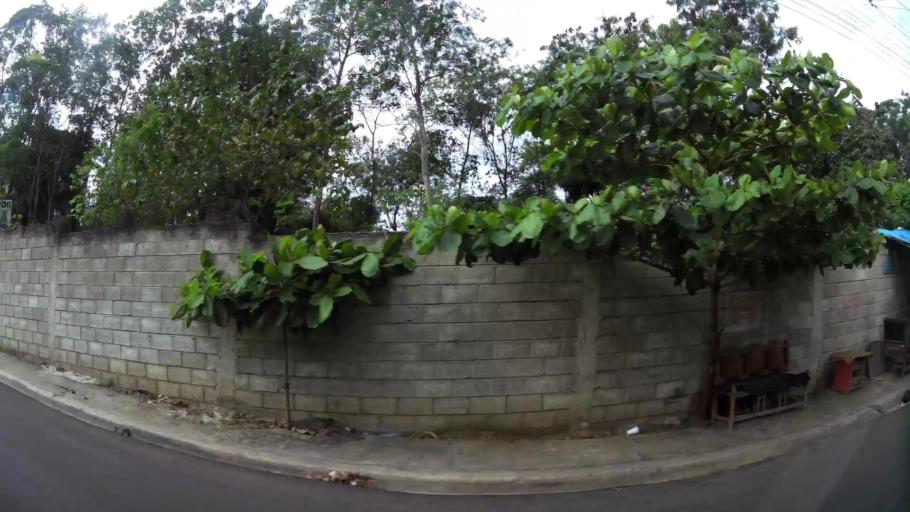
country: DO
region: Santiago
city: Santiago de los Caballeros
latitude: 19.4272
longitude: -70.6734
